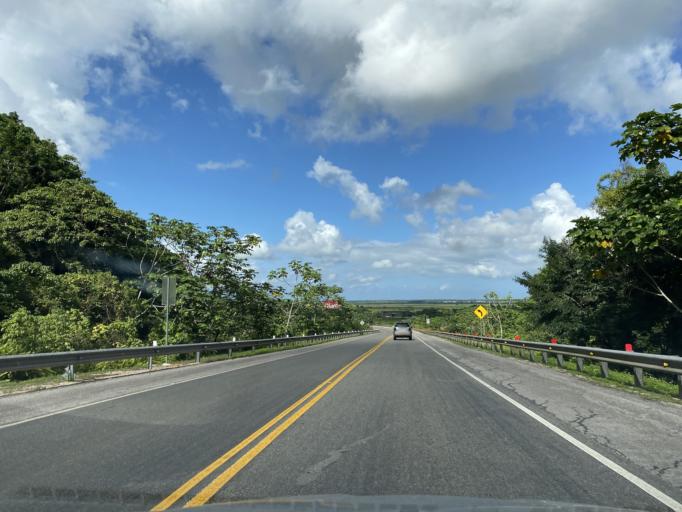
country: DO
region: Duarte
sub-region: Villa Riva
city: Agua Santa del Yuna
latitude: 19.1094
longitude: -69.8341
